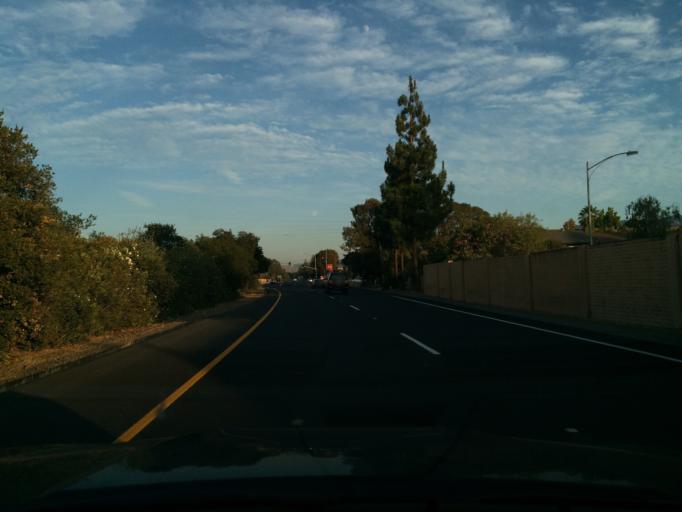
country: US
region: California
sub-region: Santa Clara County
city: Seven Trees
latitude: 37.2228
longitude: -121.8641
